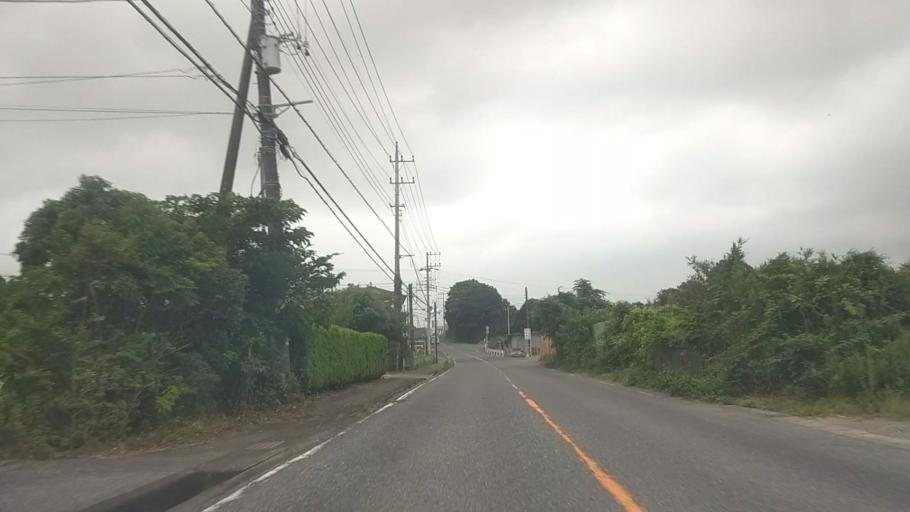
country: JP
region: Chiba
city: Kawaguchi
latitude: 35.1180
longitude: 140.0743
